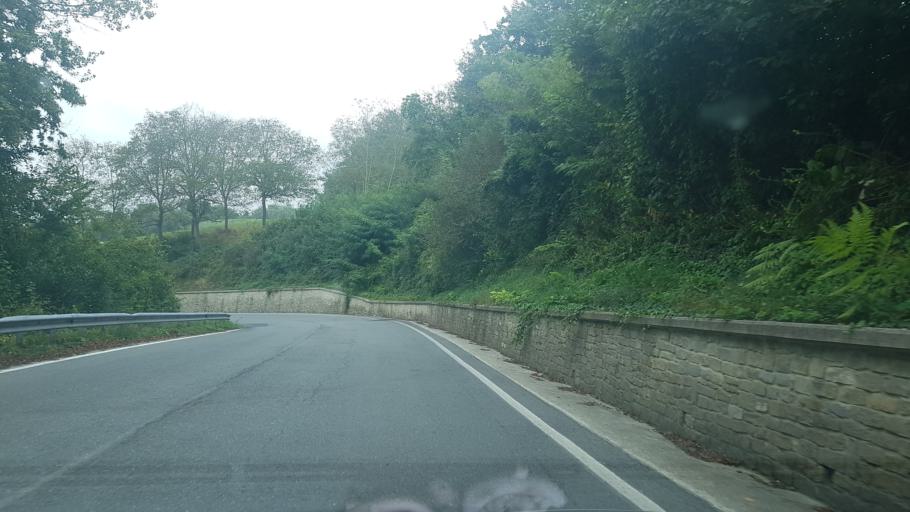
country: IT
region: Piedmont
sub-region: Provincia di Cuneo
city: Camerana
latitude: 44.4174
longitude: 8.1395
